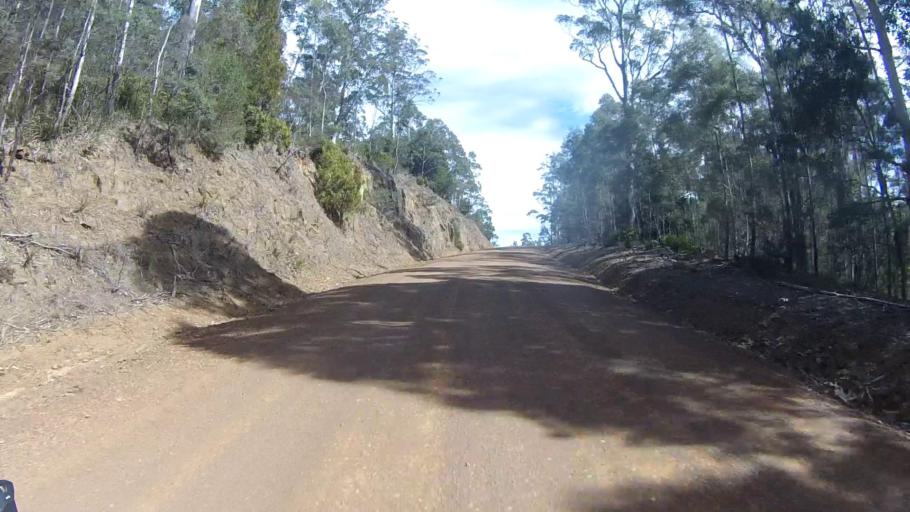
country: AU
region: Tasmania
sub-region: Sorell
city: Sorell
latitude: -42.6025
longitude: 147.8879
